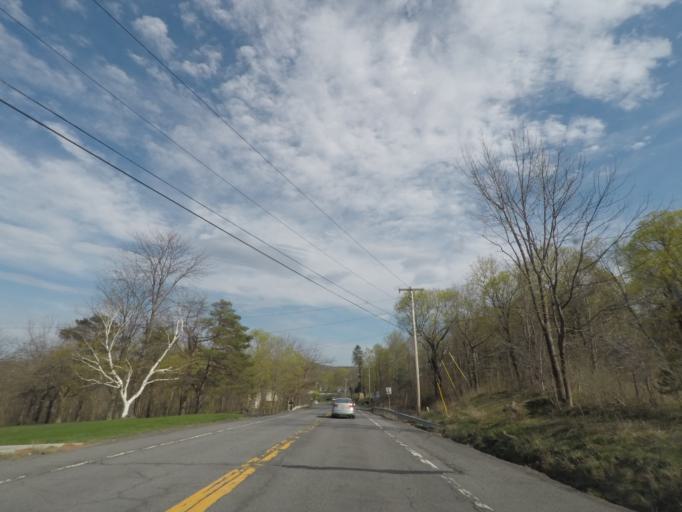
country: US
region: New York
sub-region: Albany County
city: Voorheesville
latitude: 42.6235
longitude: -73.9712
